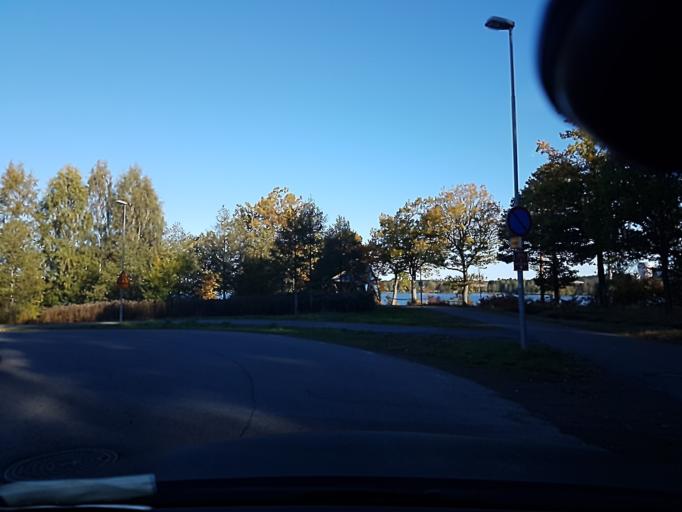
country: SE
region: Kronoberg
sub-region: Vaxjo Kommun
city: Vaexjoe
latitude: 56.8573
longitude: 14.8307
